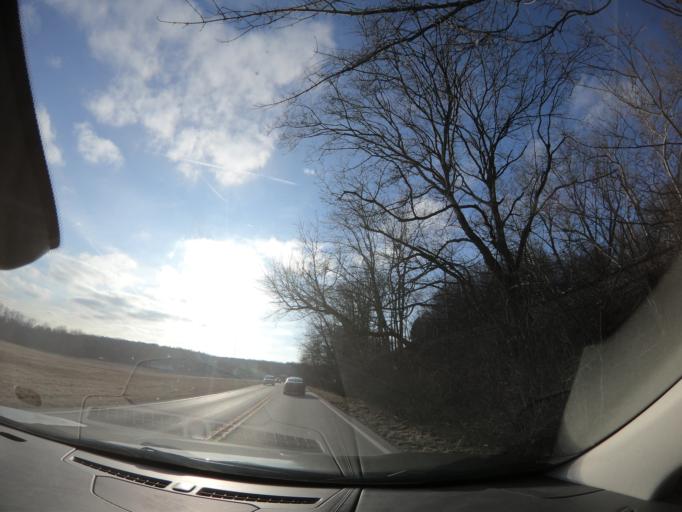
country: US
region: Kentucky
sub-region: Jefferson County
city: Middletown
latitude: 38.1915
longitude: -85.4821
